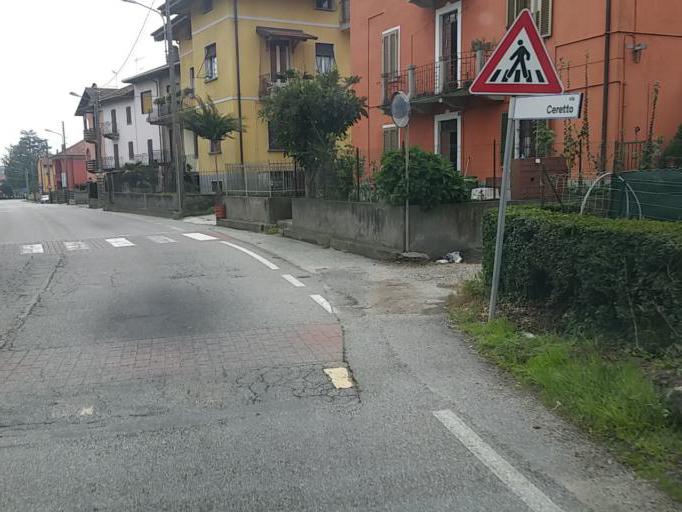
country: IT
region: Piedmont
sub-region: Provincia di Novara
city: Gozzano
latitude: 45.7537
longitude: 8.4315
